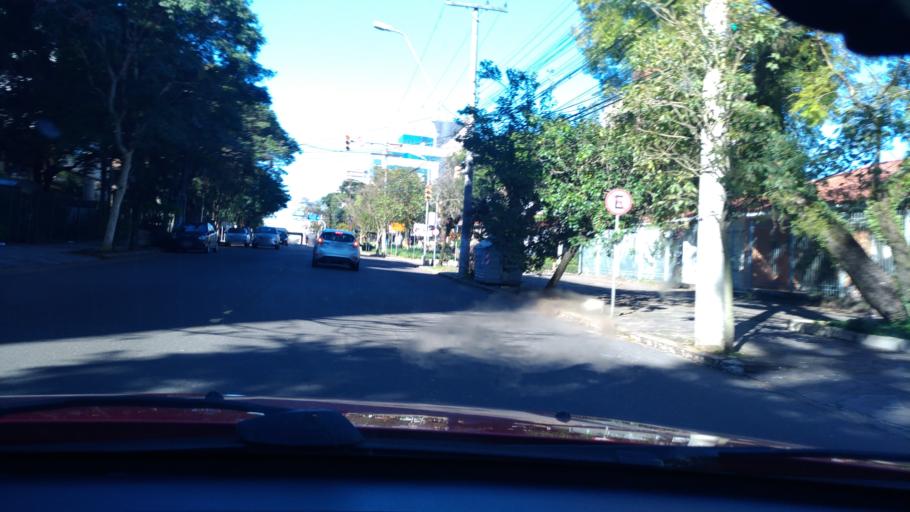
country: BR
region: Rio Grande do Sul
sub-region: Porto Alegre
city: Porto Alegre
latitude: -30.0177
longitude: -51.1902
